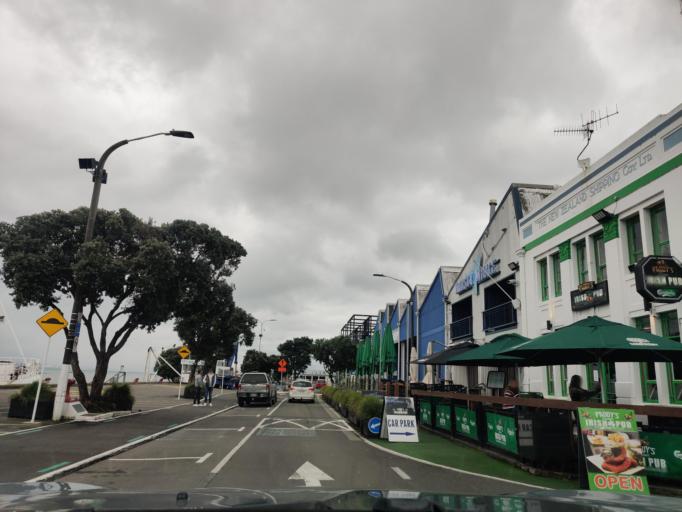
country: NZ
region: Hawke's Bay
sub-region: Napier City
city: Napier
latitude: -39.4830
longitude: 176.8943
